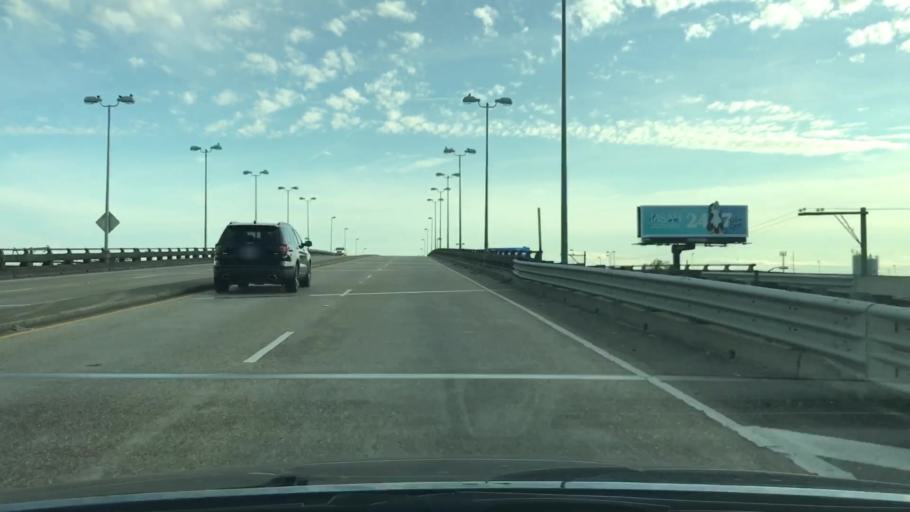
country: US
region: Louisiana
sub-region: Jefferson Parish
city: Metairie Terrace
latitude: 29.9769
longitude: -90.1564
